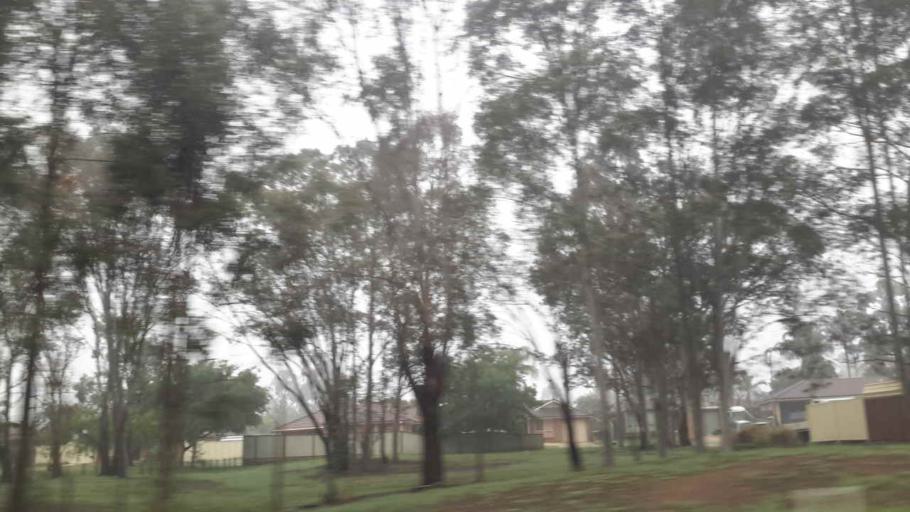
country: AU
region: New South Wales
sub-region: Penrith Municipality
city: Werrington Downs
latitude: -33.7149
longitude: 150.7247
